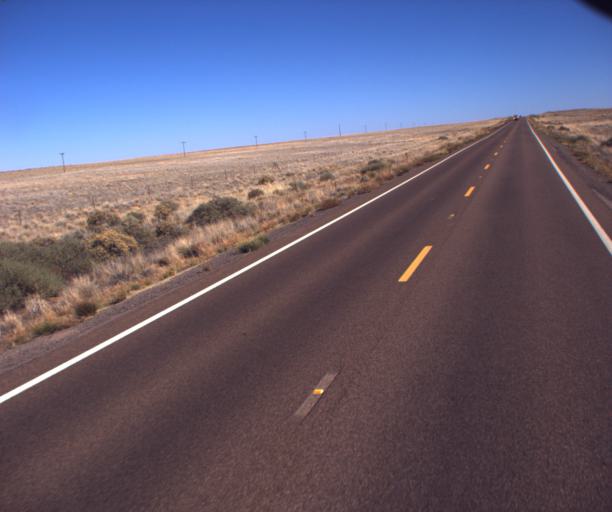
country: US
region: Arizona
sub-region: Navajo County
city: Winslow
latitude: 35.0782
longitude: -110.5624
